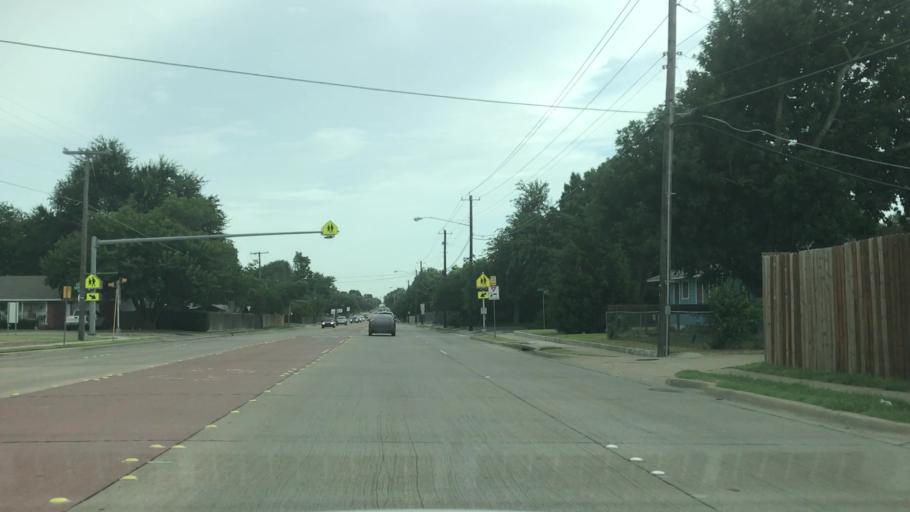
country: US
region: Texas
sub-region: Dallas County
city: Garland
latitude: 32.8759
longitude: -96.6483
